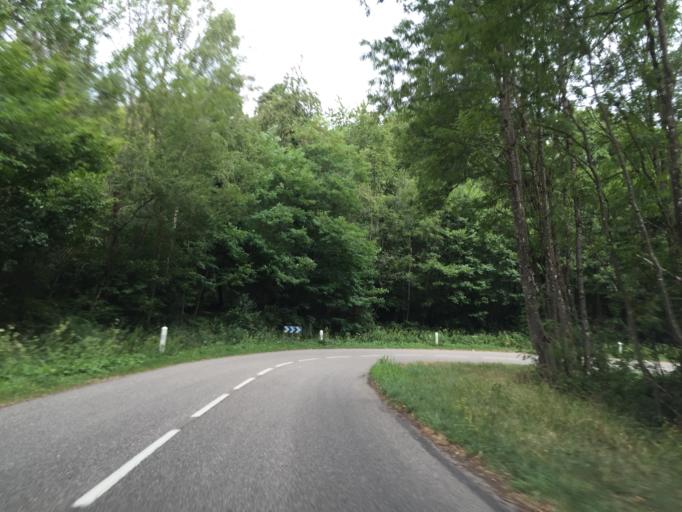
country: FR
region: Alsace
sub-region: Departement du Bas-Rhin
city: Soultz-sous-Forets
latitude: 48.9942
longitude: 7.8729
